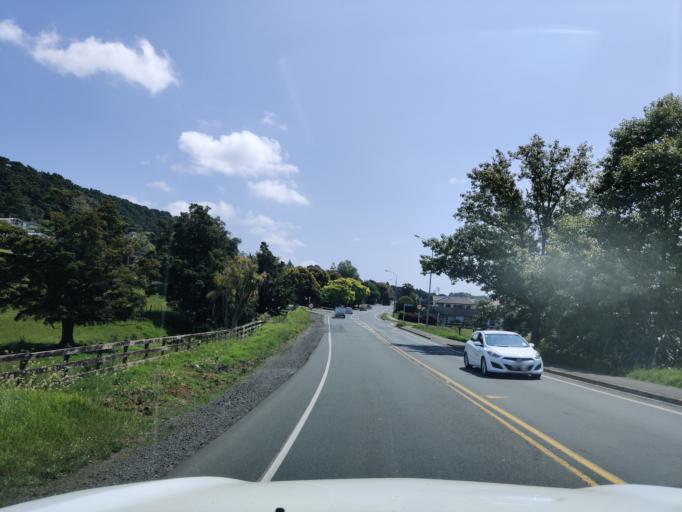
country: NZ
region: Auckland
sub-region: Auckland
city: Pukekohe East
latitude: -37.1968
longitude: 174.9193
